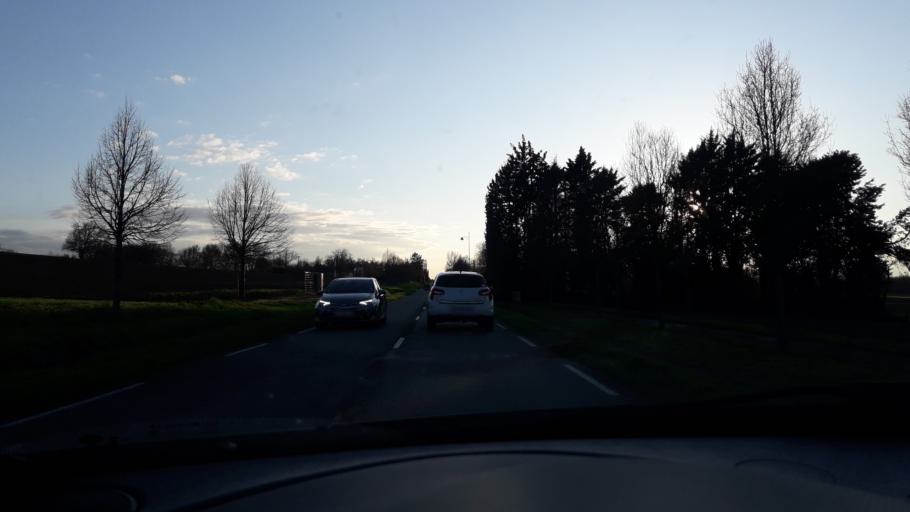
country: FR
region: Midi-Pyrenees
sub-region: Departement de la Haute-Garonne
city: Levignac
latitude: 43.6579
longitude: 1.1820
